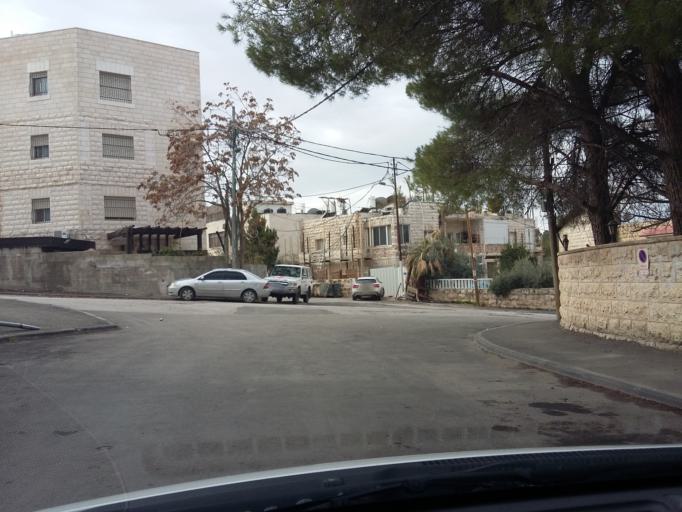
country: PS
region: West Bank
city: East Jerusalem
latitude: 31.7848
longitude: 35.2413
